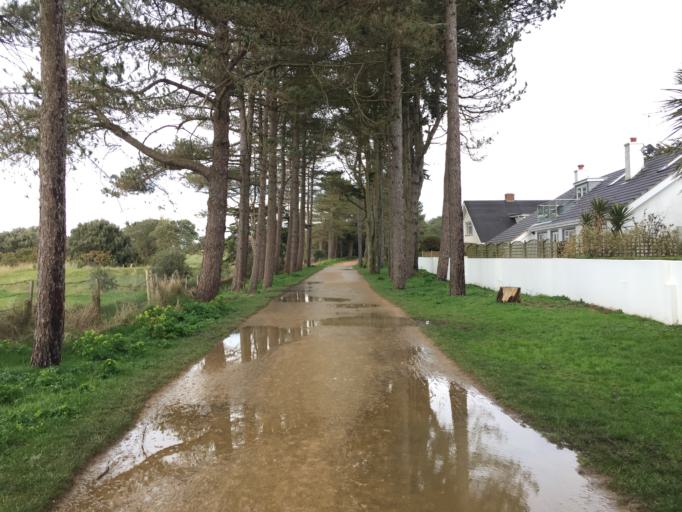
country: JE
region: St Helier
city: Saint Helier
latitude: 49.1912
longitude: -2.2129
